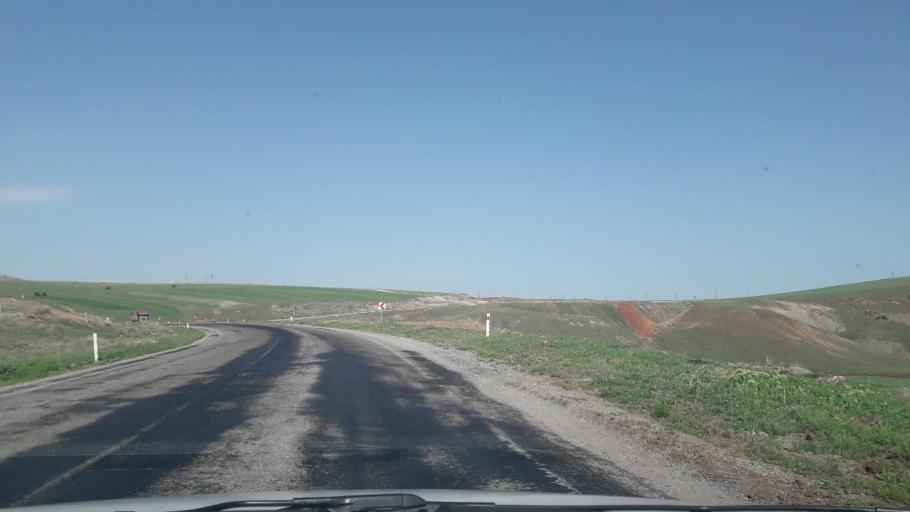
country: TR
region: Sivas
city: Kangal
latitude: 39.1663
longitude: 37.4776
